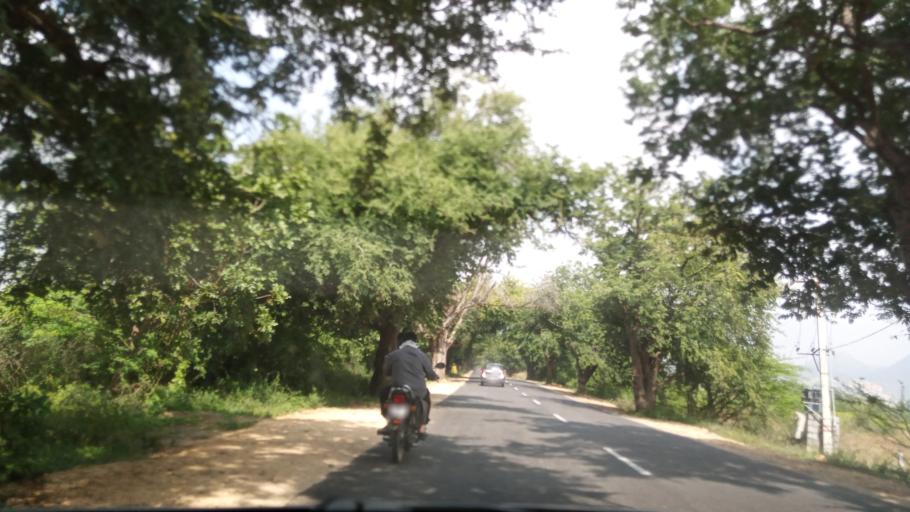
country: IN
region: Andhra Pradesh
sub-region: Chittoor
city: Madanapalle
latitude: 13.6222
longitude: 78.5473
